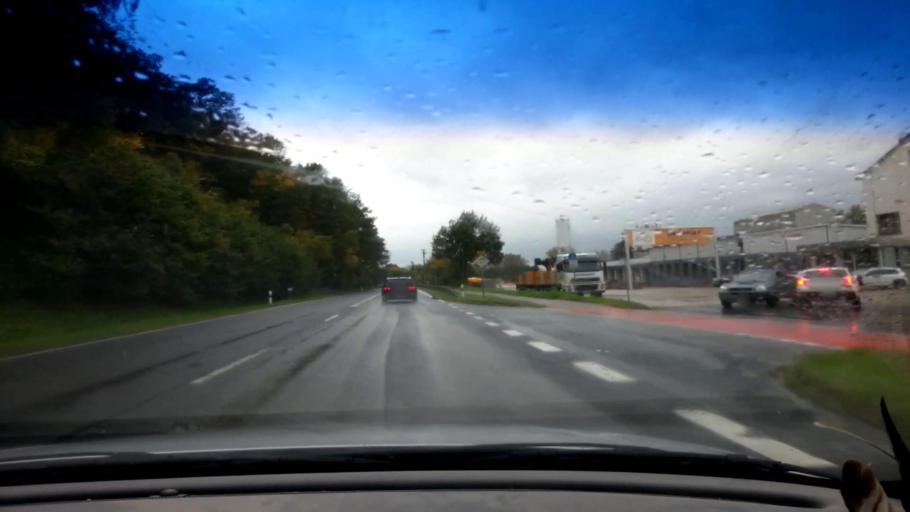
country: DE
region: Bavaria
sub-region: Upper Franconia
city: Oberhaid
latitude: 49.9201
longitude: 10.8005
